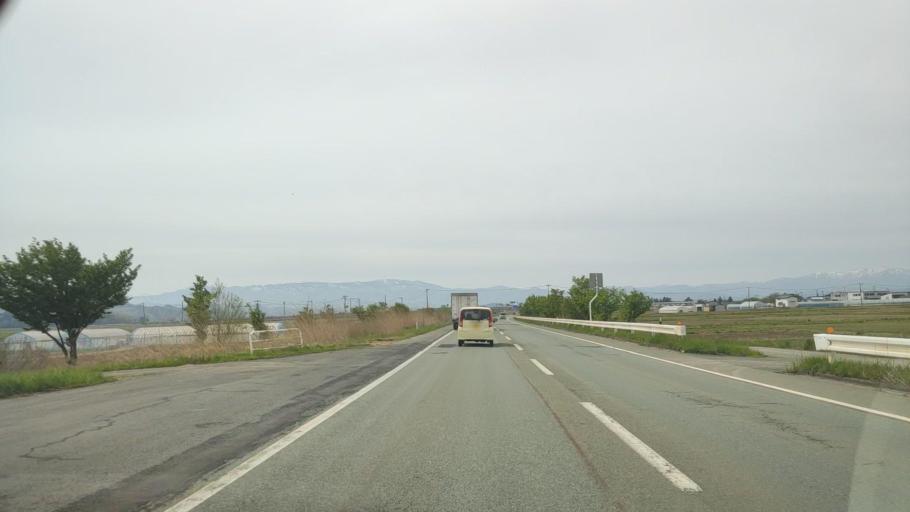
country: JP
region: Yamagata
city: Takahata
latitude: 38.0377
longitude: 140.1735
